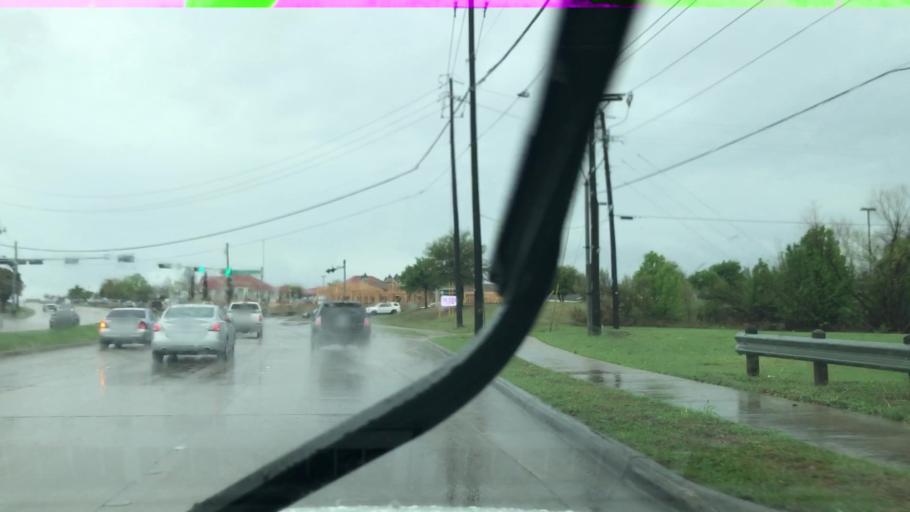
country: US
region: Texas
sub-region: Denton County
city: The Colony
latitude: 33.0363
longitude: -96.8843
